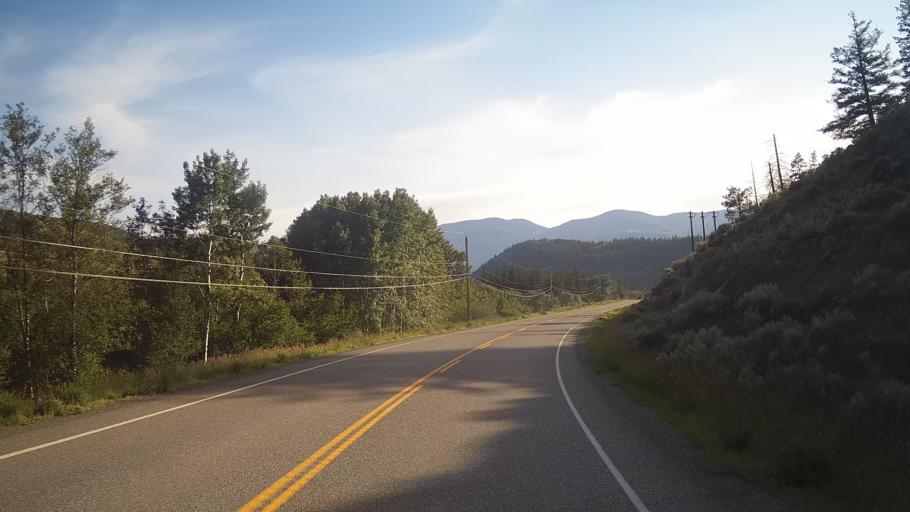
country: CA
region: British Columbia
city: Lillooet
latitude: 50.8877
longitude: -121.8117
